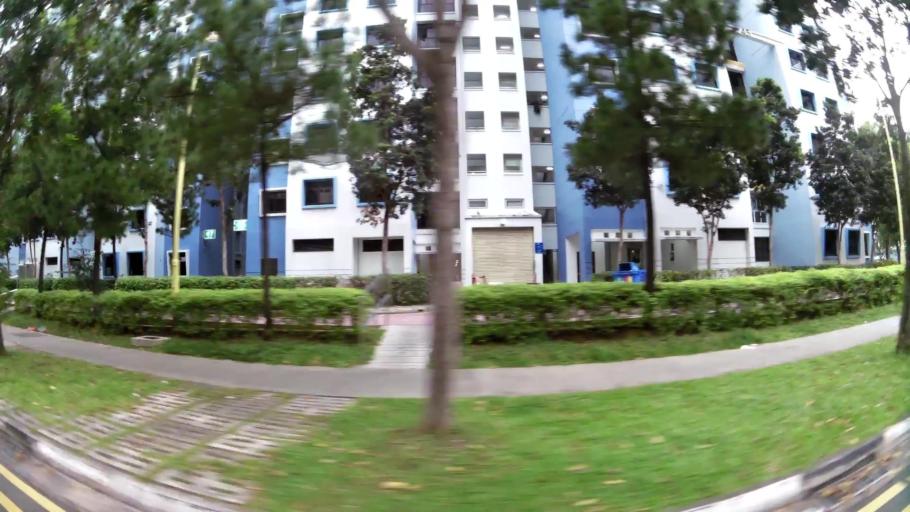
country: SG
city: Singapore
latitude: 1.3089
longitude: 103.8845
